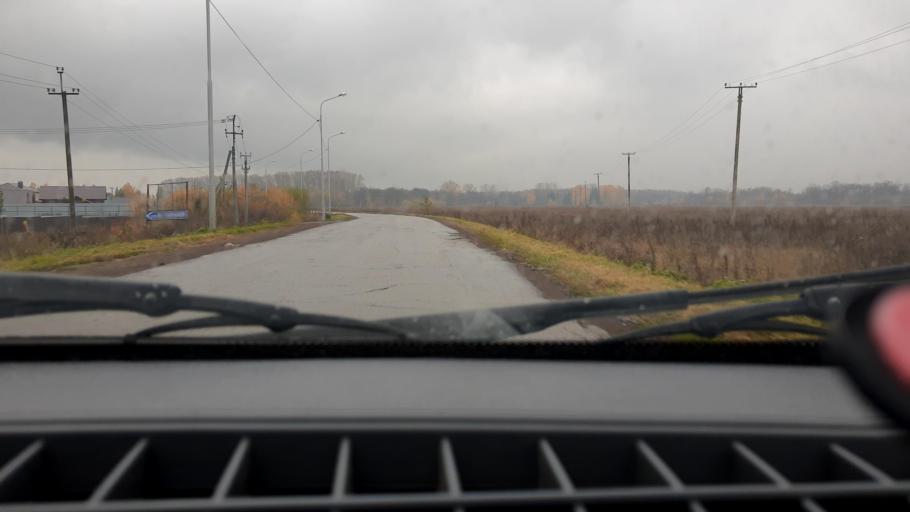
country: RU
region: Bashkortostan
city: Ufa
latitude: 54.6579
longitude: 55.9175
